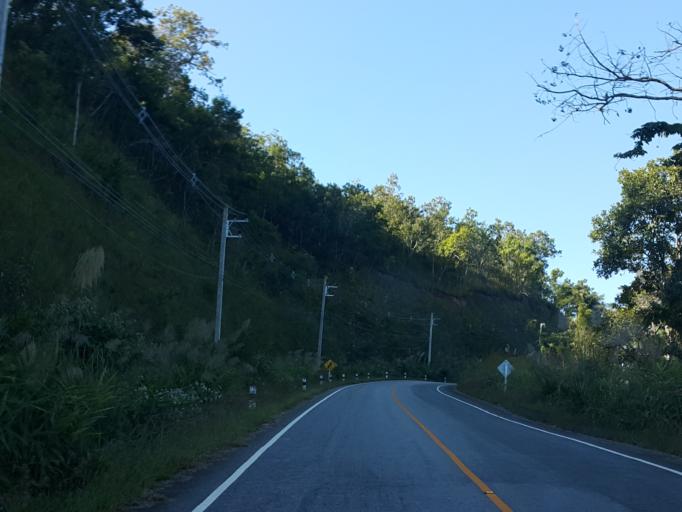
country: TH
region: Chiang Mai
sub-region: Amphoe Chiang Dao
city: Chiang Dao
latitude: 19.5284
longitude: 98.8766
